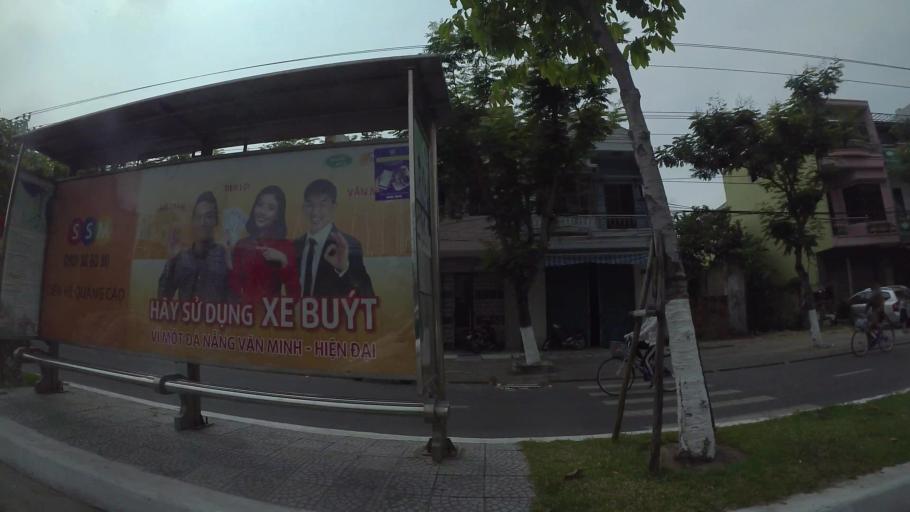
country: VN
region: Da Nang
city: Da Nang
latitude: 16.0960
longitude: 108.2449
